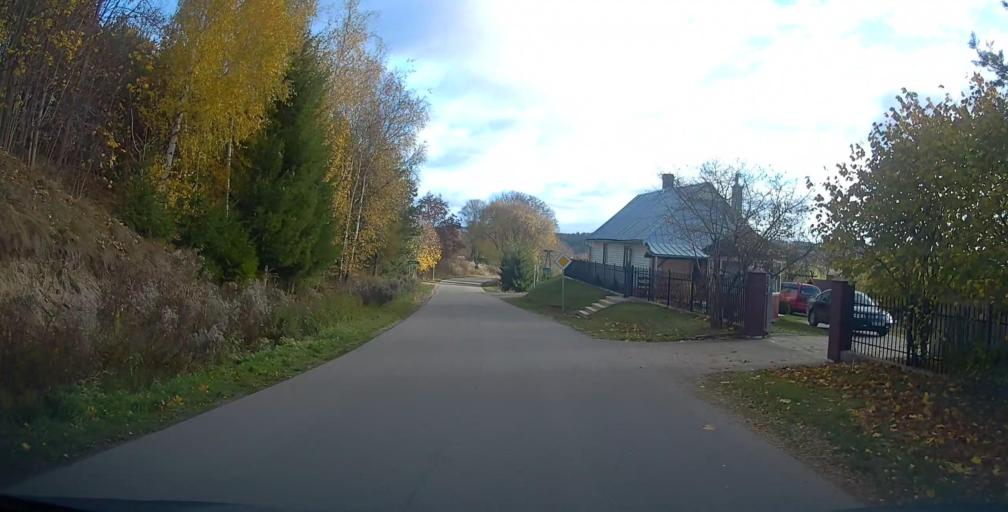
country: PL
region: Podlasie
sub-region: Suwalki
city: Suwalki
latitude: 54.2833
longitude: 22.9014
